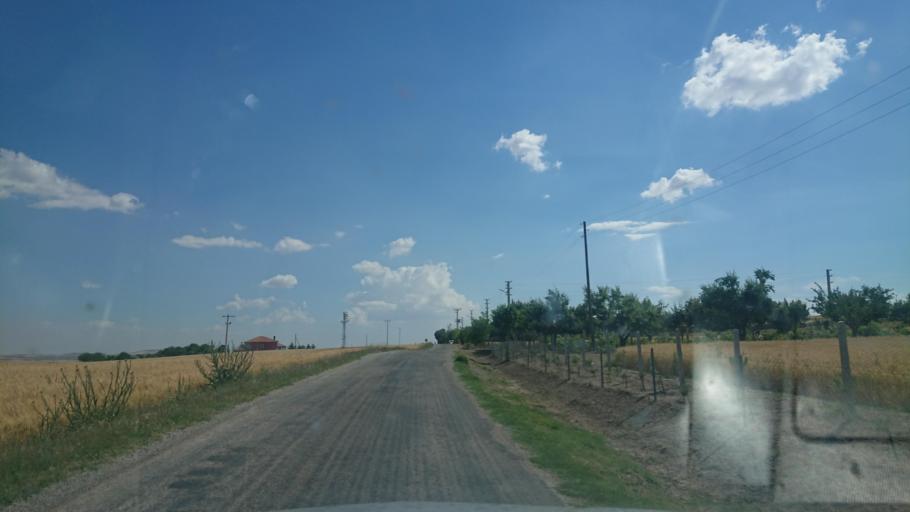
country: TR
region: Aksaray
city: Agacoren
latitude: 38.7594
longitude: 33.7823
